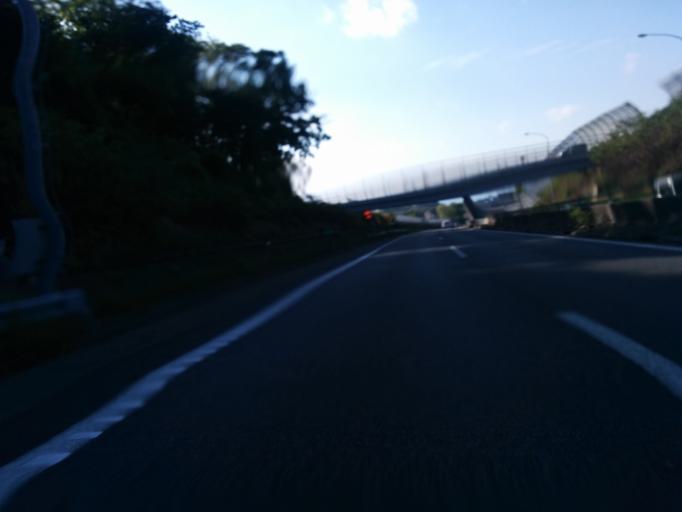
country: JP
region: Shiga Prefecture
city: Otsu-shi
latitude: 34.9940
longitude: 135.8745
